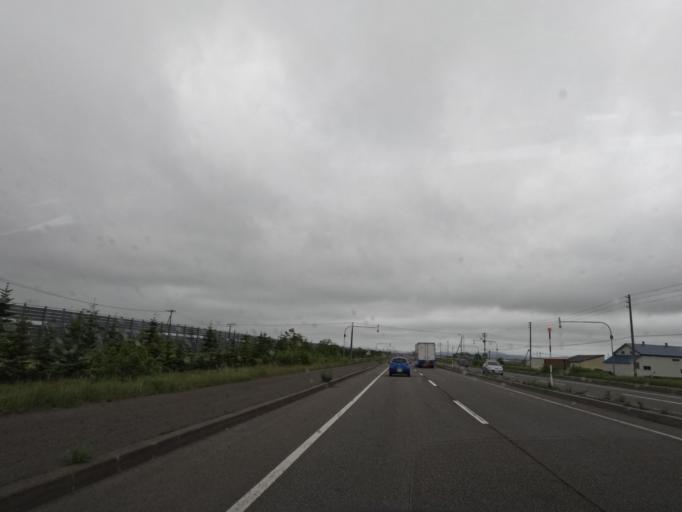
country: JP
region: Hokkaido
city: Tobetsu
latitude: 43.1672
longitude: 141.5205
